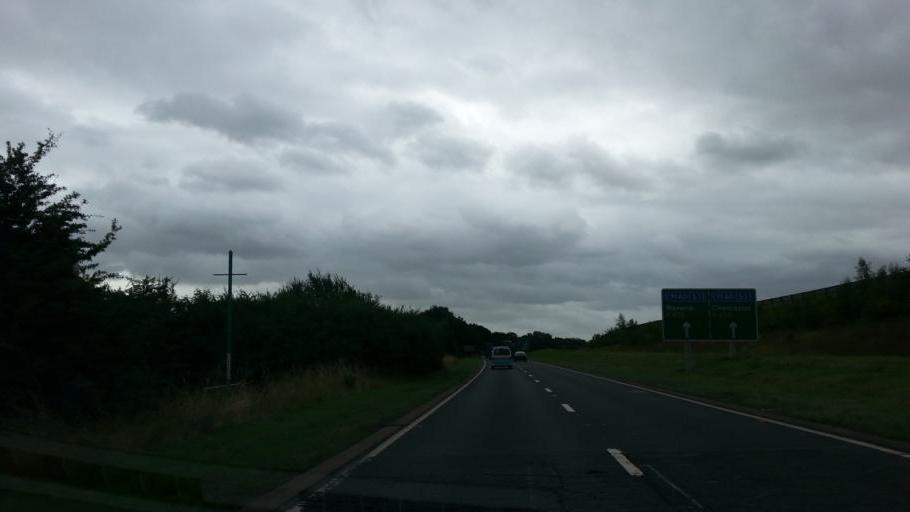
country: GB
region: England
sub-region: Warwickshire
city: Warwick
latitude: 52.2672
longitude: -1.6126
